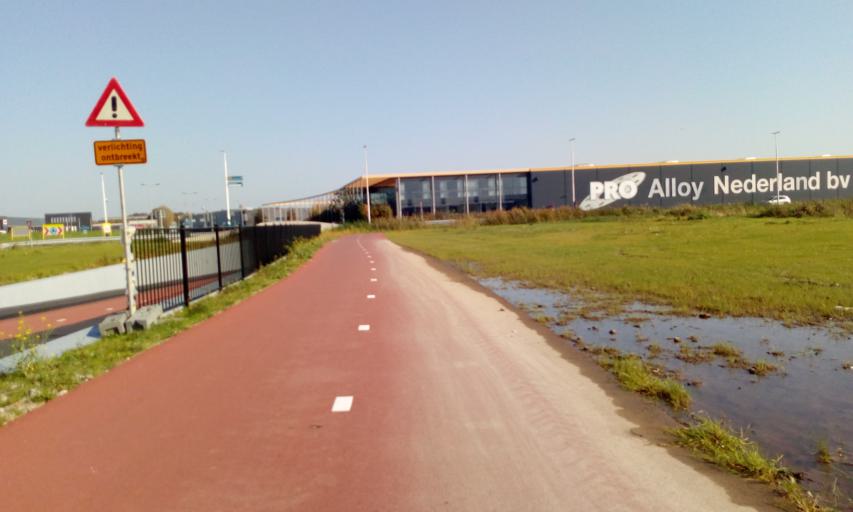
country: NL
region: South Holland
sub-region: Gemeente Lansingerland
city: Berkel en Rodenrijs
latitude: 51.9759
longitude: 4.4485
